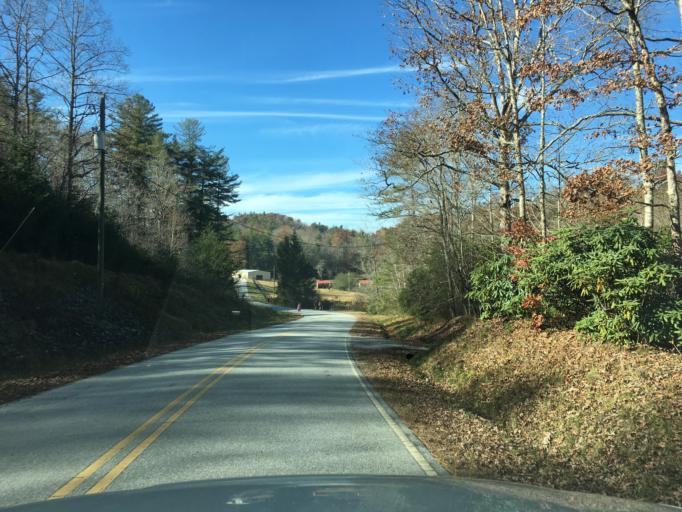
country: US
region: North Carolina
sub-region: Henderson County
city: Etowah
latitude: 35.2237
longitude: -82.5902
